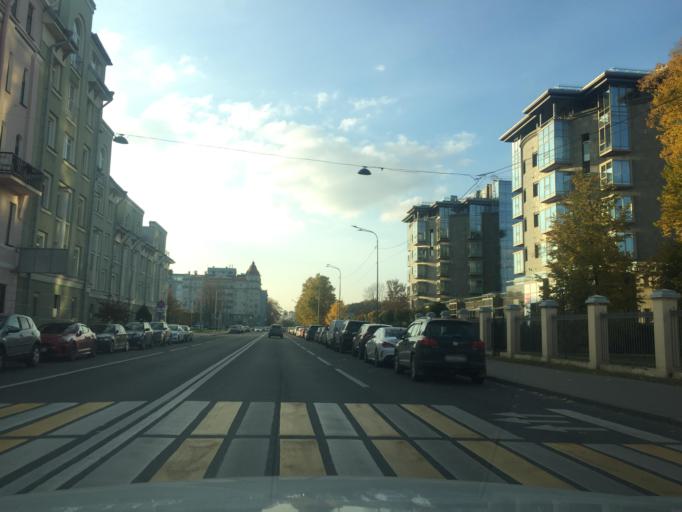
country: RU
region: Leningrad
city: Krestovskiy ostrov
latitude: 59.9728
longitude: 30.2692
